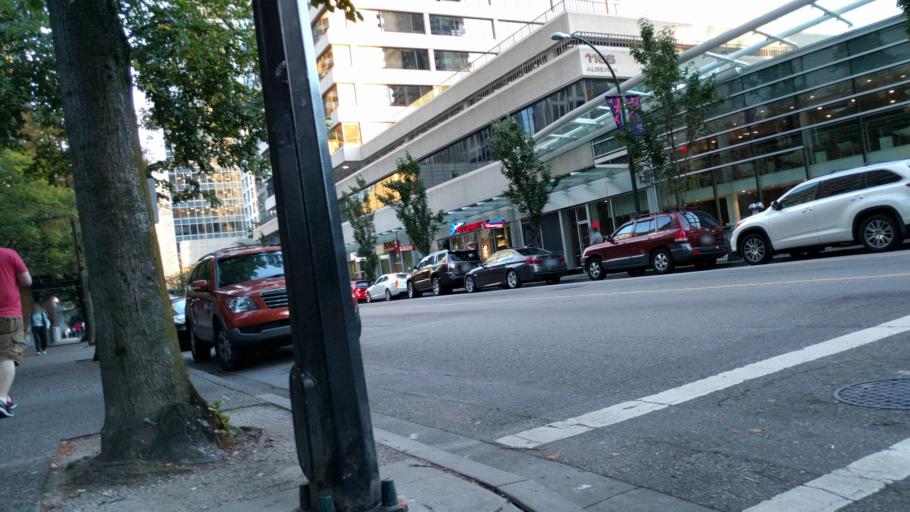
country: CA
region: British Columbia
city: West End
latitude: 49.2867
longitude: -123.1258
